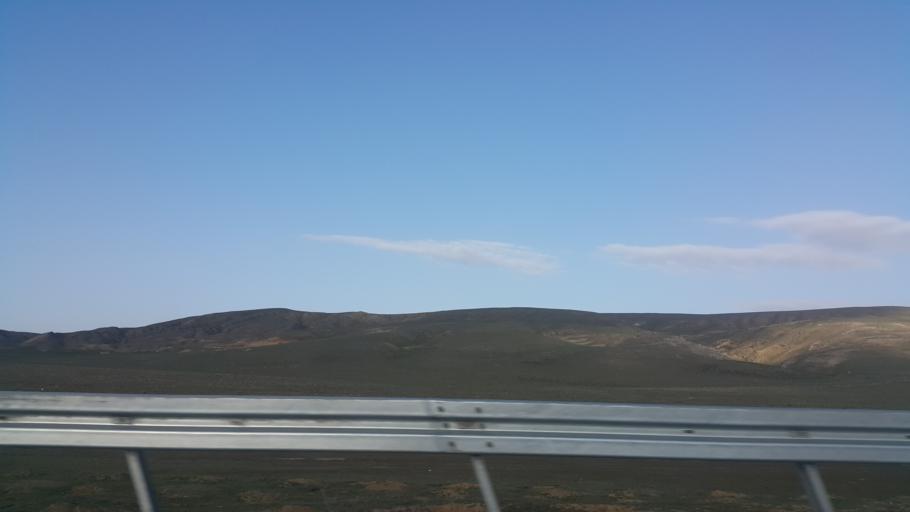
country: TR
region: Konya
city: Kulu
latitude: 39.1369
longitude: 33.3409
